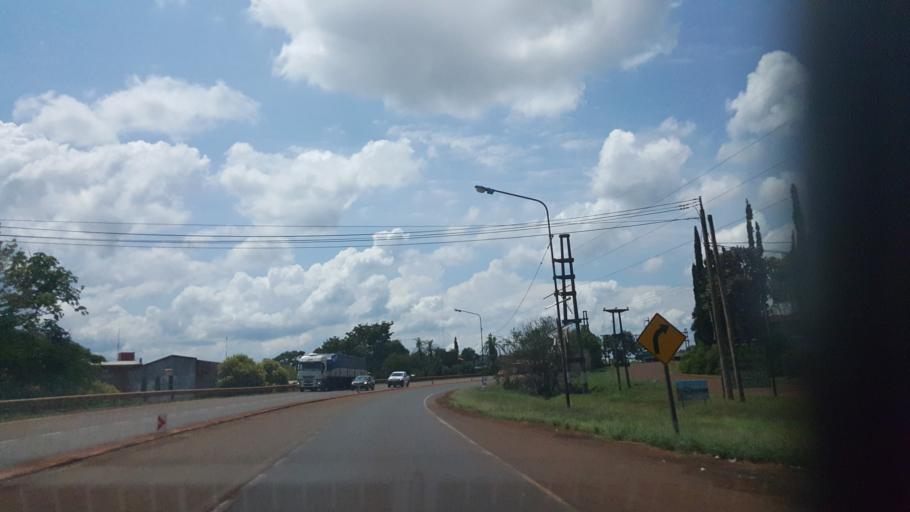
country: AR
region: Misiones
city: Puerto Rico
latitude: -26.8222
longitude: -55.0275
